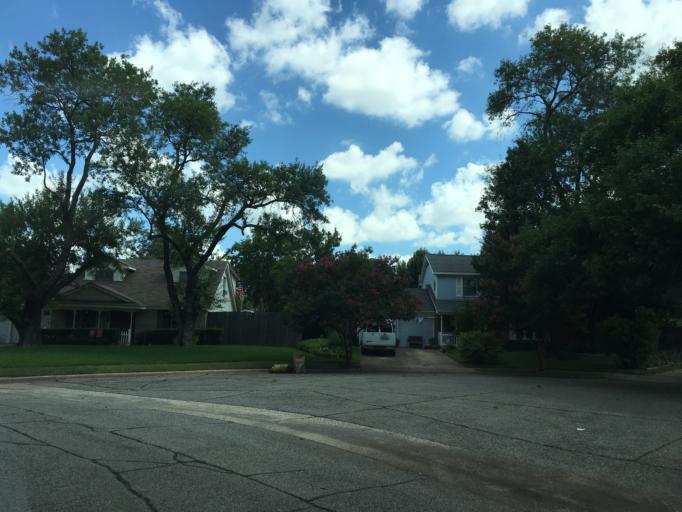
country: US
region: Texas
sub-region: Dallas County
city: Farmers Branch
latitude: 32.9265
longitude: -96.8786
